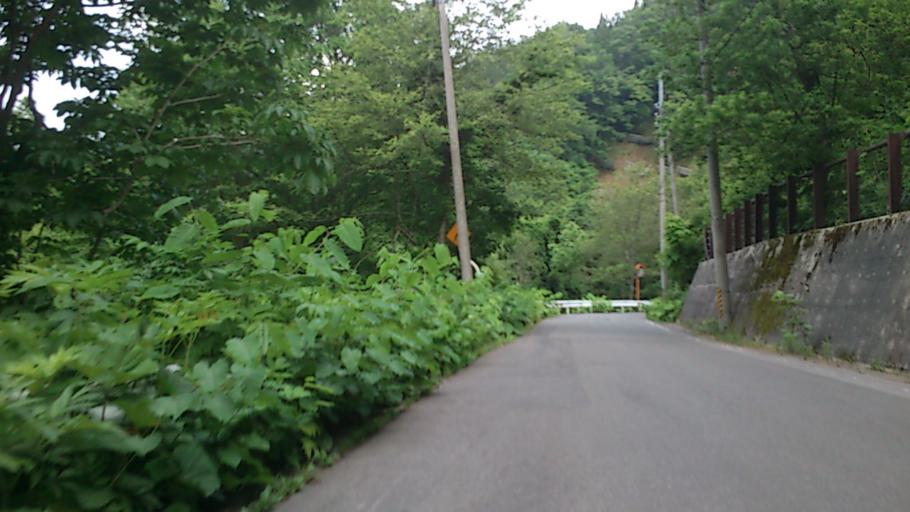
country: JP
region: Aomori
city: Hirosaki
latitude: 40.5178
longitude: 140.1793
